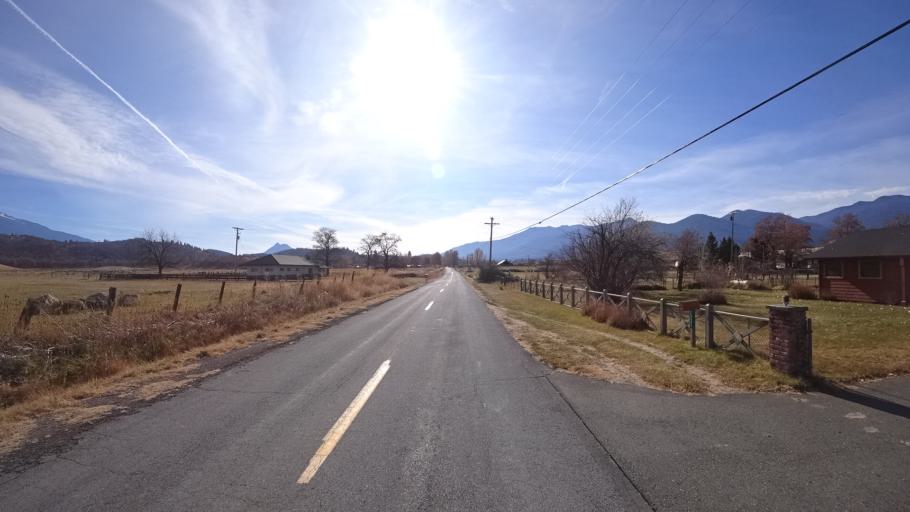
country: US
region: California
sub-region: Siskiyou County
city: Weed
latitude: 41.4657
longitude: -122.4344
